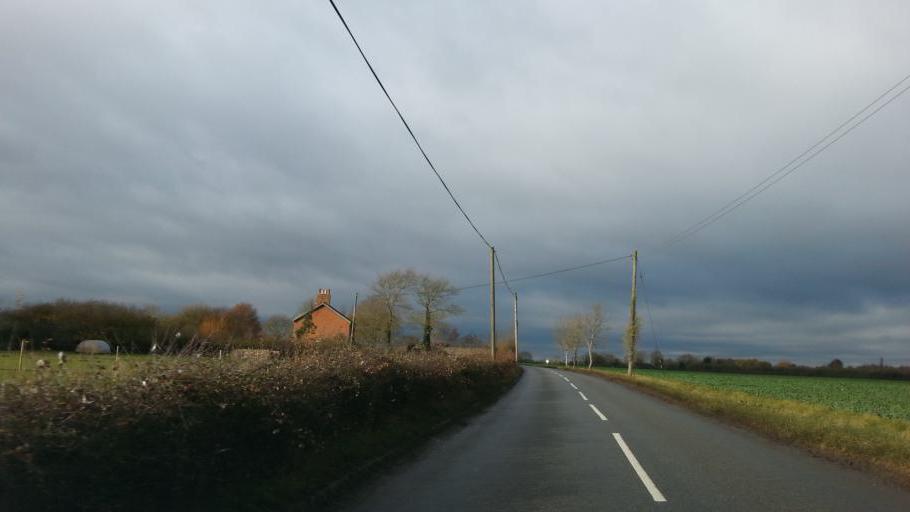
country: GB
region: England
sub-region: Suffolk
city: Framlingham
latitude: 52.3063
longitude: 1.3454
